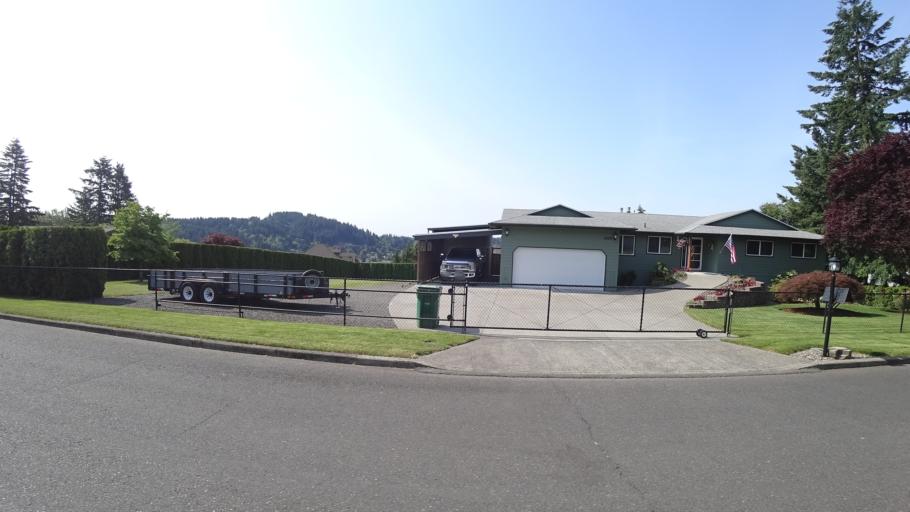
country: US
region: Oregon
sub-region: Clackamas County
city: Happy Valley
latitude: 45.4583
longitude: -122.5193
